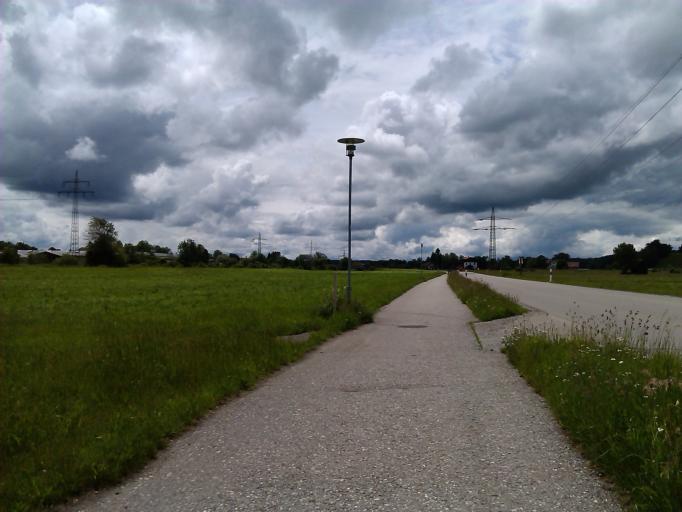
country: DE
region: Bavaria
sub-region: Swabia
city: Biessenhofen
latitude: 47.8218
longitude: 10.6274
